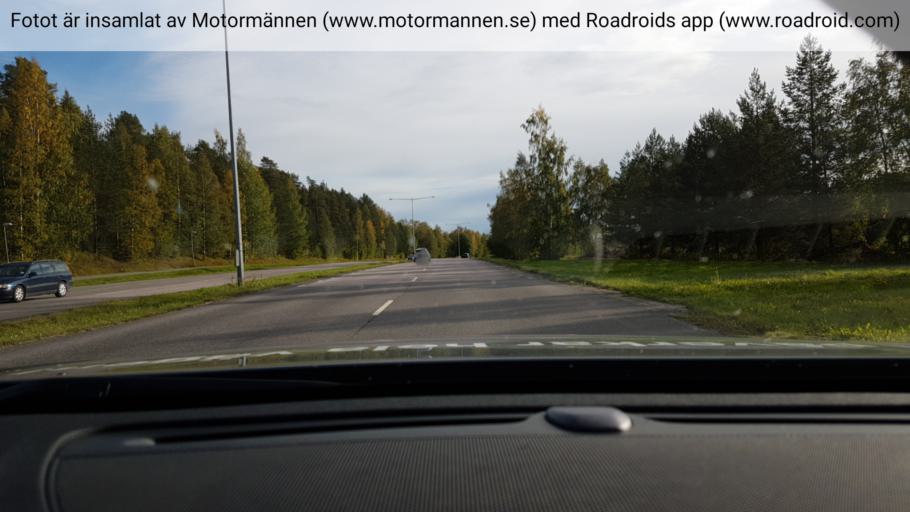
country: SE
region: Norrbotten
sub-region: Lulea Kommun
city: Lulea
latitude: 65.6094
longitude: 22.1365
